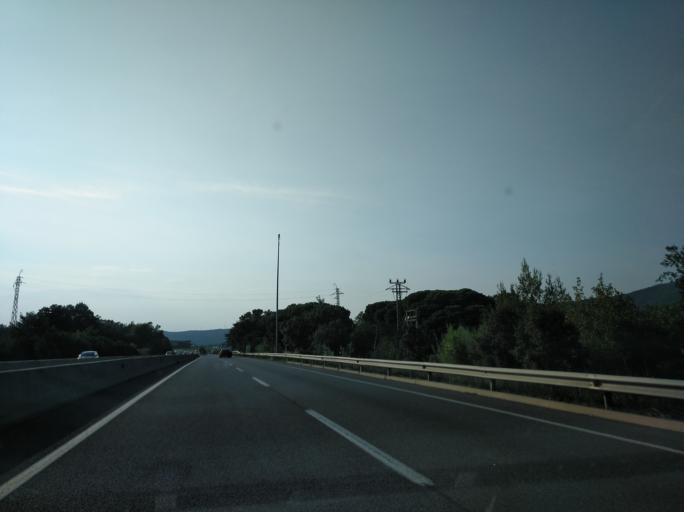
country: ES
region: Catalonia
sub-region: Provincia de Girona
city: Santa Cristina d'Aro
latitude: 41.8117
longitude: 2.9928
